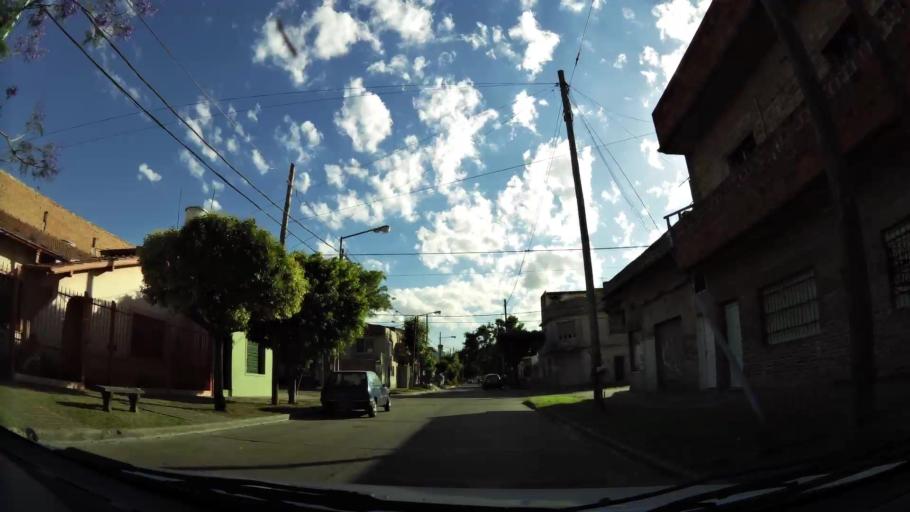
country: AR
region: Buenos Aires
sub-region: Partido de General San Martin
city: General San Martin
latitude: -34.5359
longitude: -58.5555
